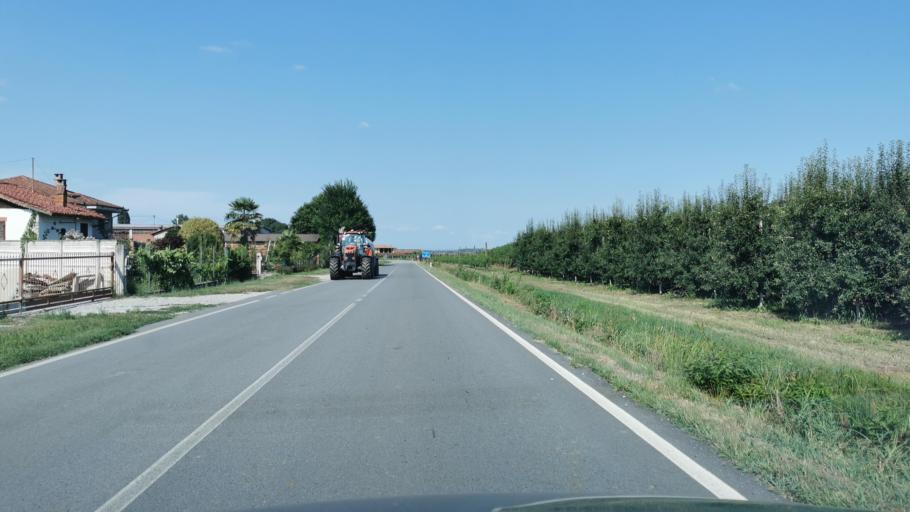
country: IT
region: Piedmont
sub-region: Provincia di Cuneo
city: Revello
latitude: 44.6769
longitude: 7.4081
